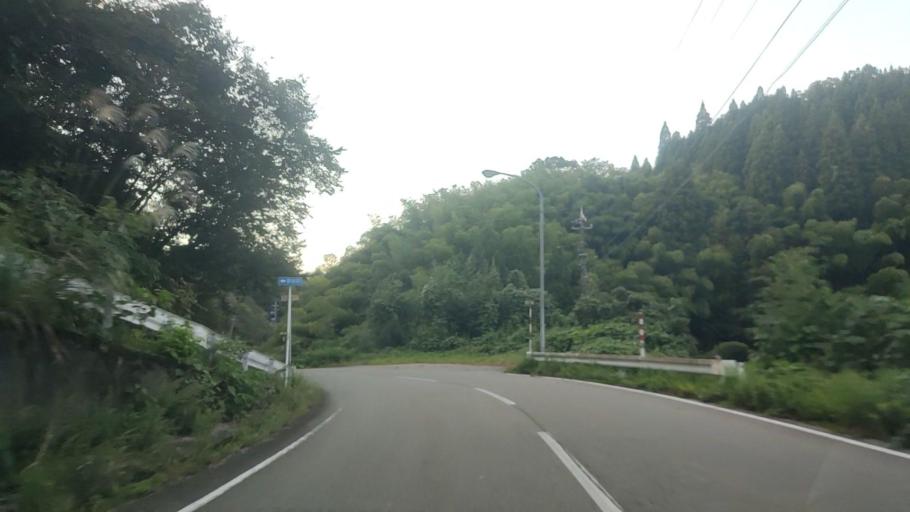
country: JP
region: Ishikawa
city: Tsubata
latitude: 36.6324
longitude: 136.7711
